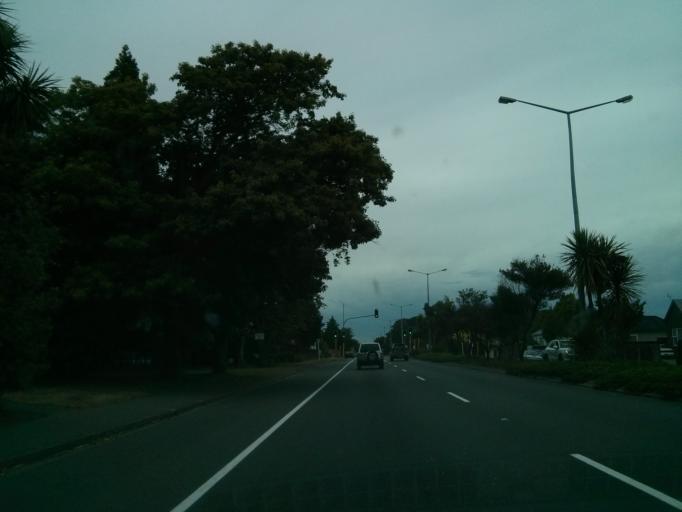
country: NZ
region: Canterbury
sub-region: Waimakariri District
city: Kaiapoi
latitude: -43.4525
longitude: 172.6277
